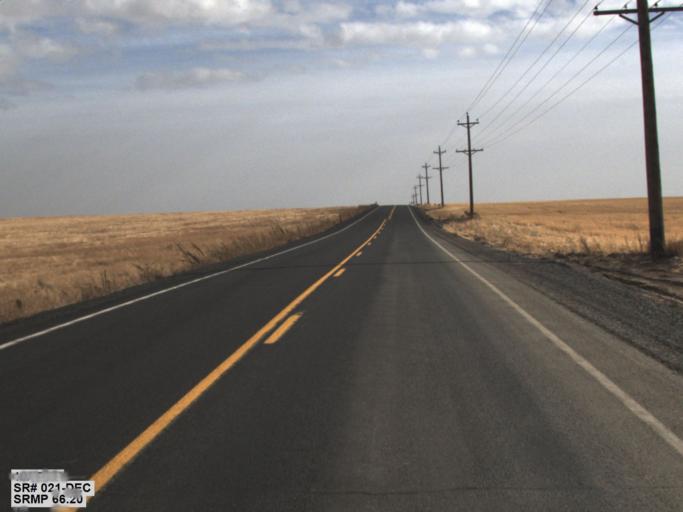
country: US
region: Washington
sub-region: Adams County
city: Ritzville
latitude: 47.4544
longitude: -118.7492
